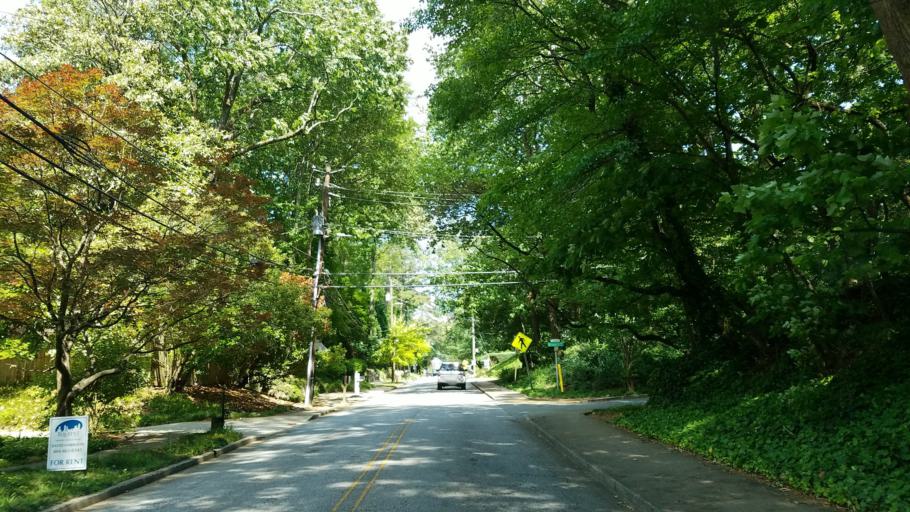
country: US
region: Georgia
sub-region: DeKalb County
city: North Atlanta
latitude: 33.8228
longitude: -84.3822
